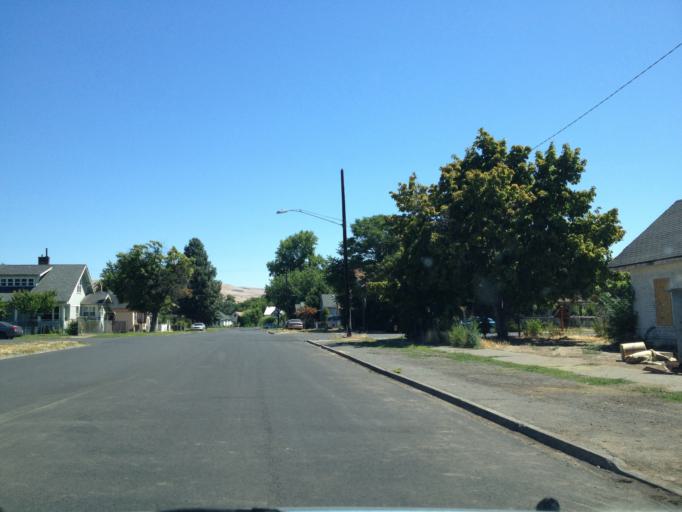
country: US
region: Washington
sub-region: Yakima County
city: Yakima
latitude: 46.6017
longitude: -120.4964
